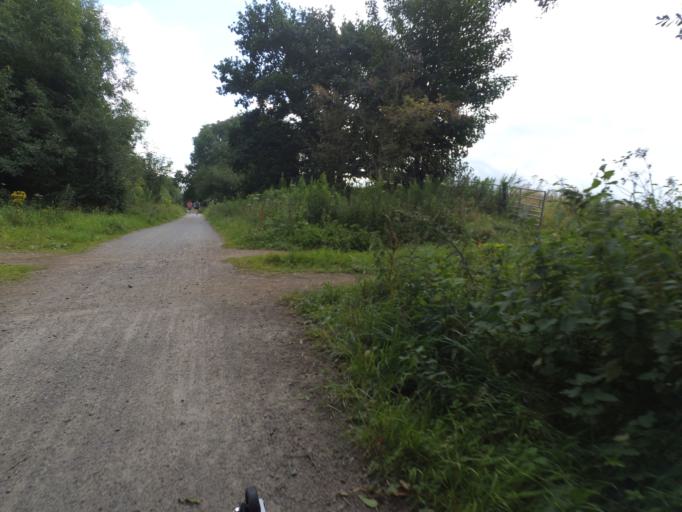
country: GB
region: England
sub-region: Shropshire
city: Woodcote
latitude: 52.7625
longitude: -2.3314
